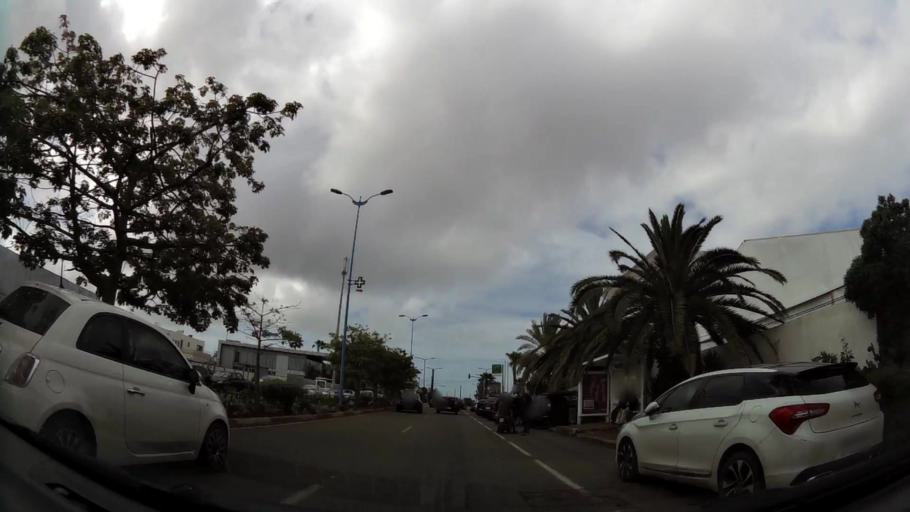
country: MA
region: Grand Casablanca
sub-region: Casablanca
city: Casablanca
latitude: 33.5457
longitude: -7.6315
